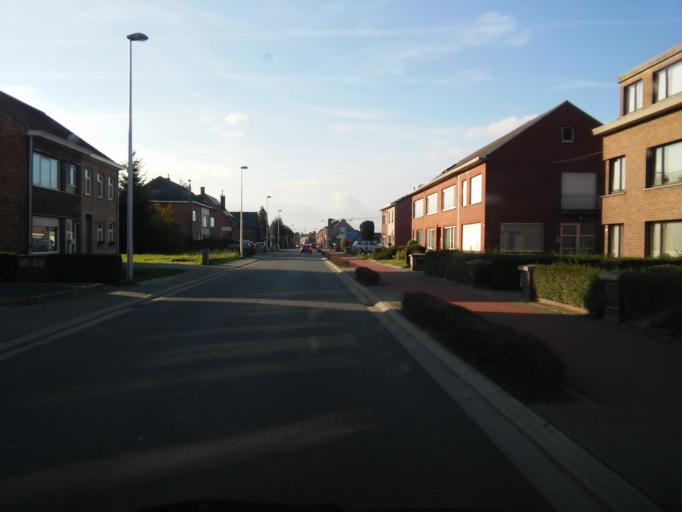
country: BE
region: Flanders
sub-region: Provincie Antwerpen
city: Duffel
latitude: 51.0933
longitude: 4.5220
